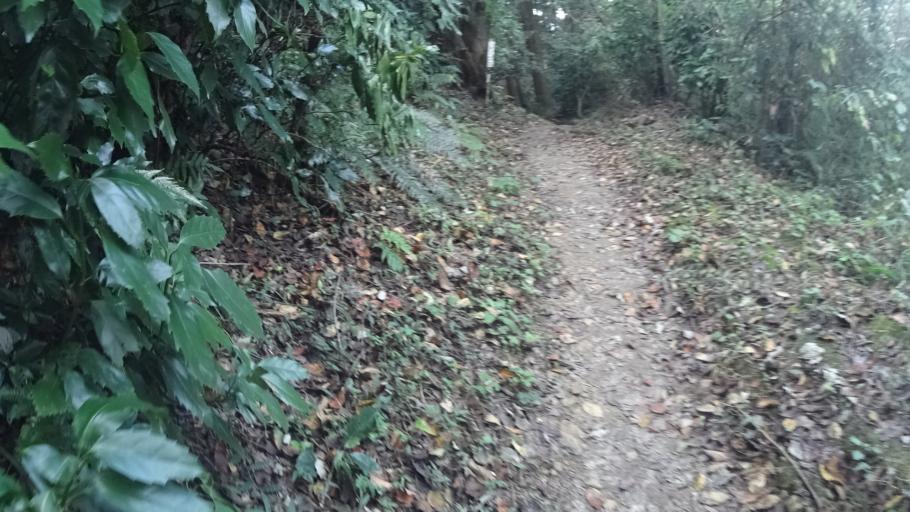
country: JP
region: Kanagawa
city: Zushi
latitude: 35.2876
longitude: 139.6133
